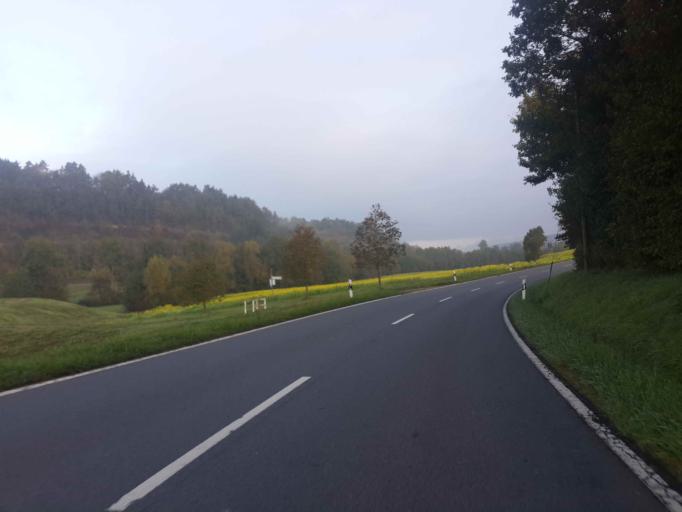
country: DE
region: Baden-Wuerttemberg
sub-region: Regierungsbezirk Stuttgart
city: Bad Mergentheim
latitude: 49.4654
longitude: 9.7754
